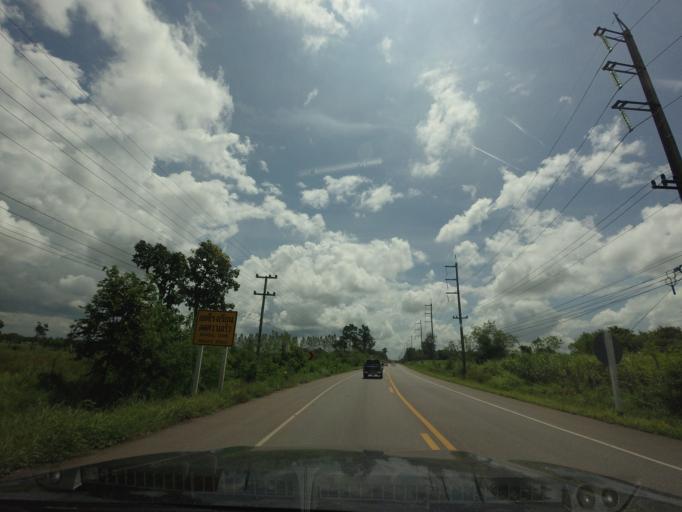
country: TH
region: Changwat Udon Thani
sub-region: Amphoe Ban Phue
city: Ban Phue
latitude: 17.6512
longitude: 102.5198
